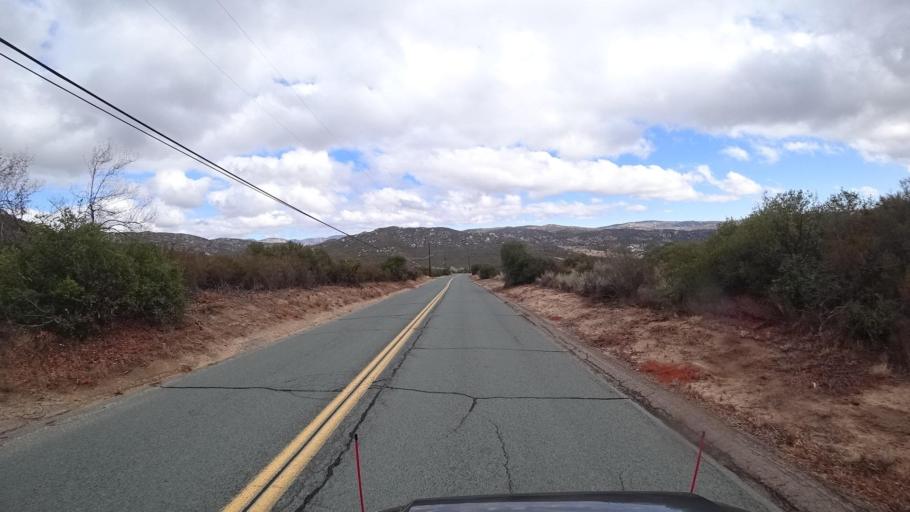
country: US
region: California
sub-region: San Diego County
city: Campo
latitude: 32.6754
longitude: -116.4297
